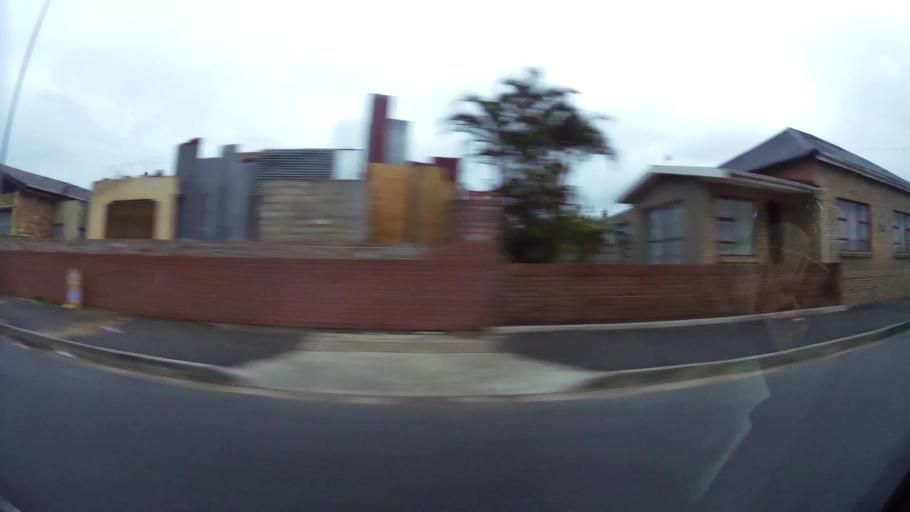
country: ZA
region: Eastern Cape
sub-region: Nelson Mandela Bay Metropolitan Municipality
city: Port Elizabeth
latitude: -33.9336
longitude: 25.5826
